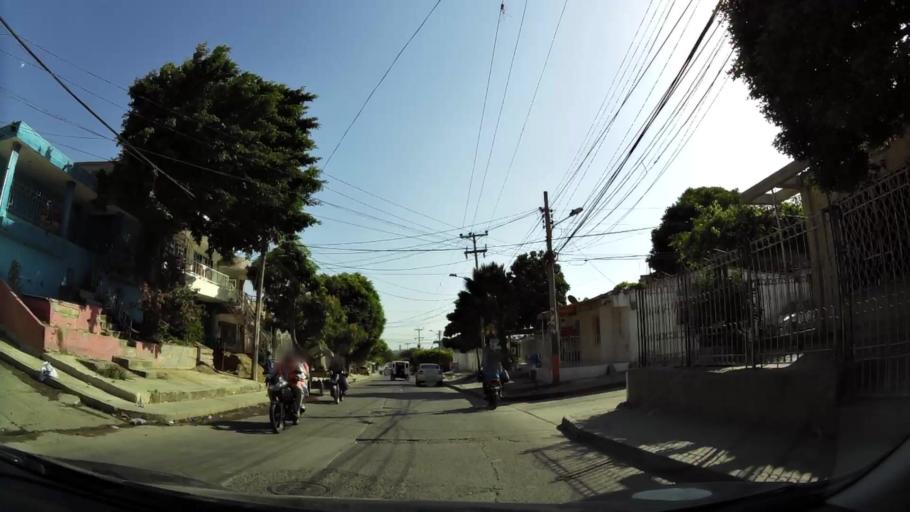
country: CO
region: Bolivar
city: Cartagena
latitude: 10.4255
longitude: -75.5201
